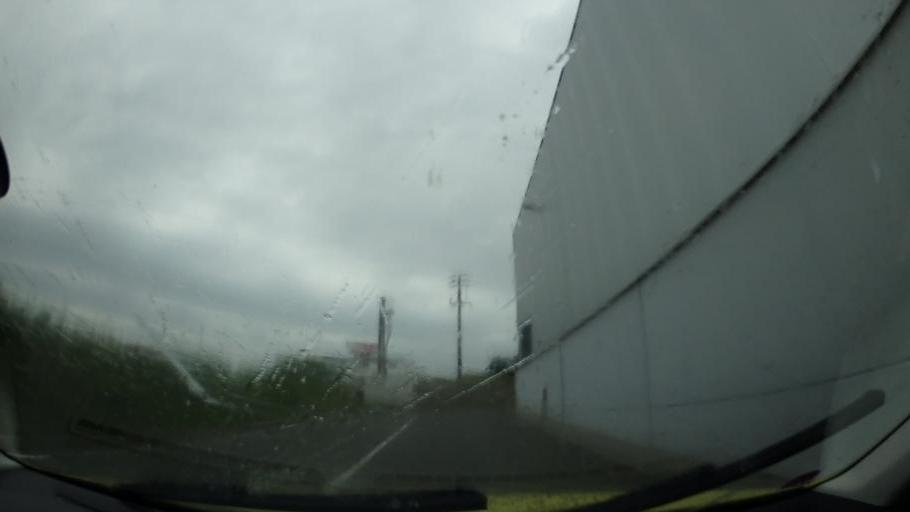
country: CZ
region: Olomoucky
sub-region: Okres Prerov
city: Hranice
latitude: 49.5579
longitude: 17.7421
